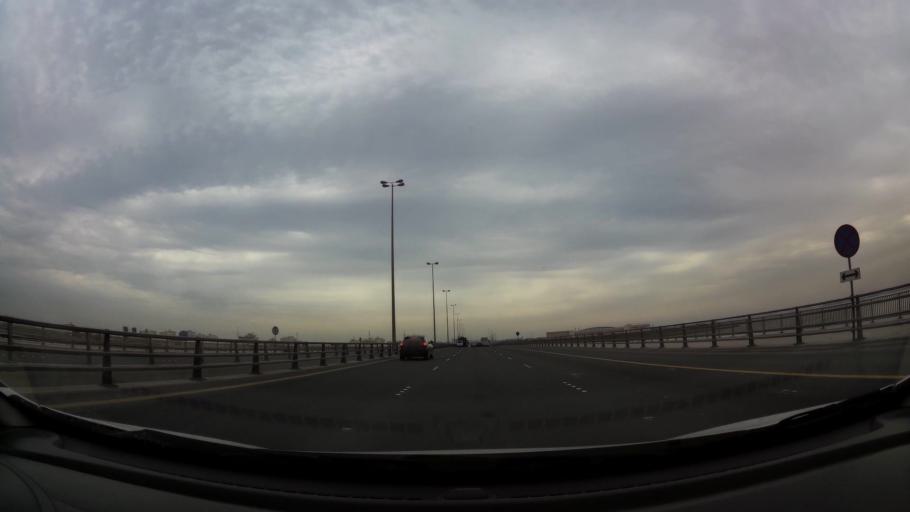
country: BH
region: Northern
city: Sitrah
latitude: 26.1757
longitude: 50.5960
